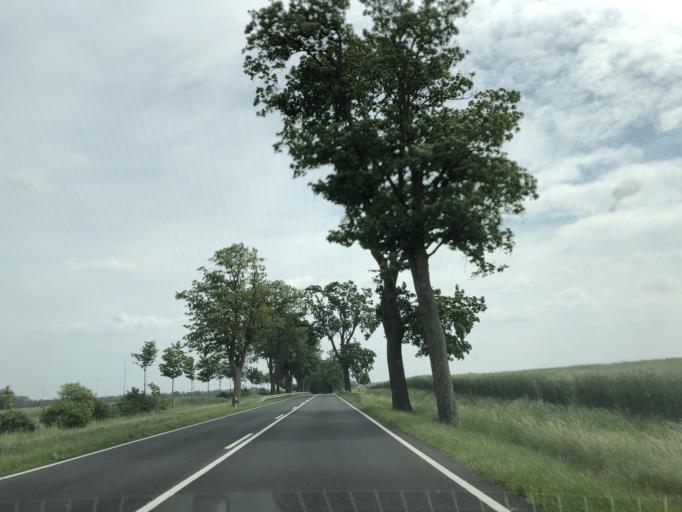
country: DE
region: Brandenburg
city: Gumtow
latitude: 52.9764
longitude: 12.2637
